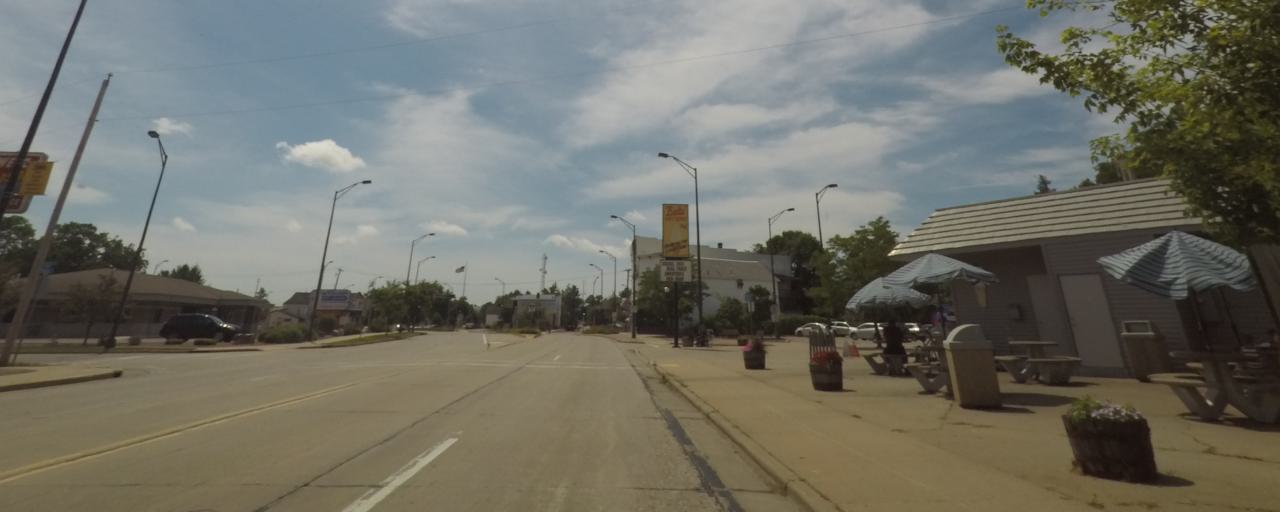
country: US
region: Wisconsin
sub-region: Portage County
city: Stevens Point
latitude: 44.5161
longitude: -89.5749
